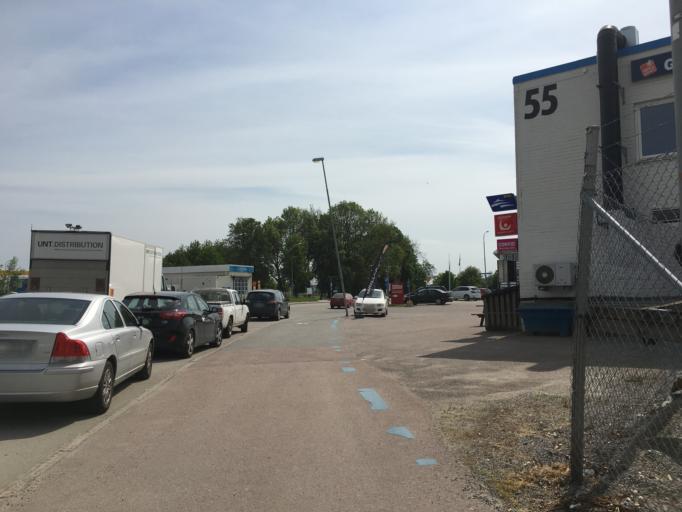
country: SE
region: Uppsala
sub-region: Uppsala Kommun
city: Uppsala
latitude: 59.8475
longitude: 17.6746
